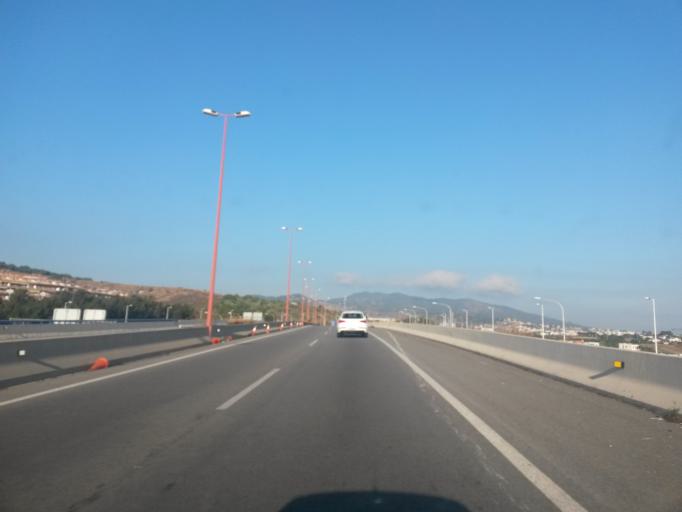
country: ES
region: Catalonia
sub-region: Provincia de Barcelona
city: Montgat
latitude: 41.4743
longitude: 2.2831
